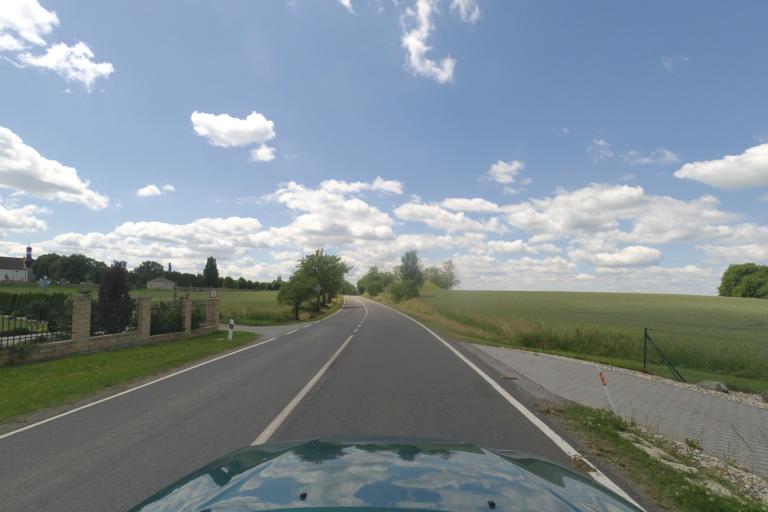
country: CZ
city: Dobruska
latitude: 50.3004
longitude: 16.1729
